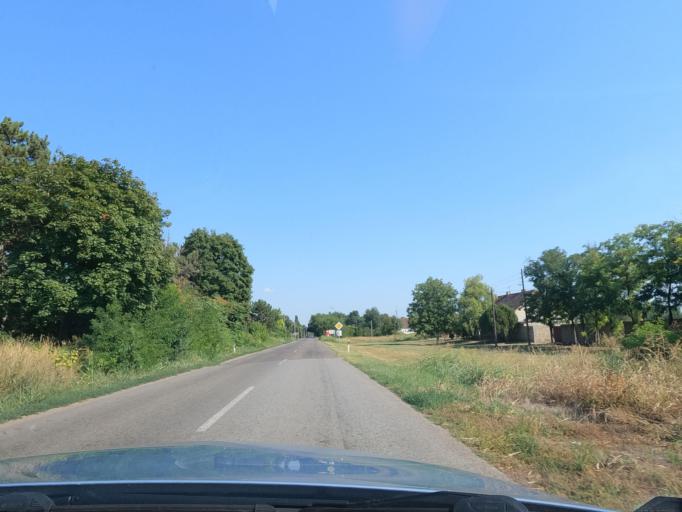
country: RS
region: Autonomna Pokrajina Vojvodina
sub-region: Juznobacki Okrug
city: Becej
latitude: 45.6317
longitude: 20.0152
